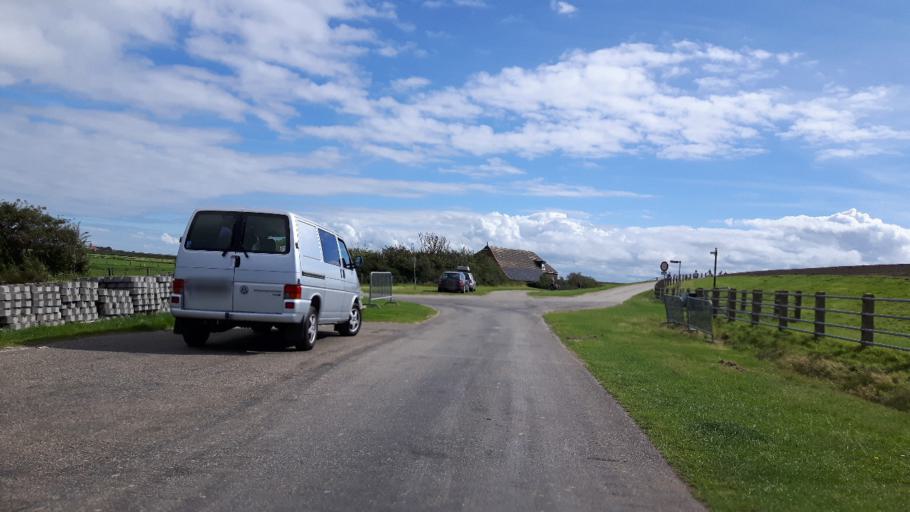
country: NL
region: Friesland
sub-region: Gemeente Ameland
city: Hollum
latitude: 53.4346
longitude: 5.6284
